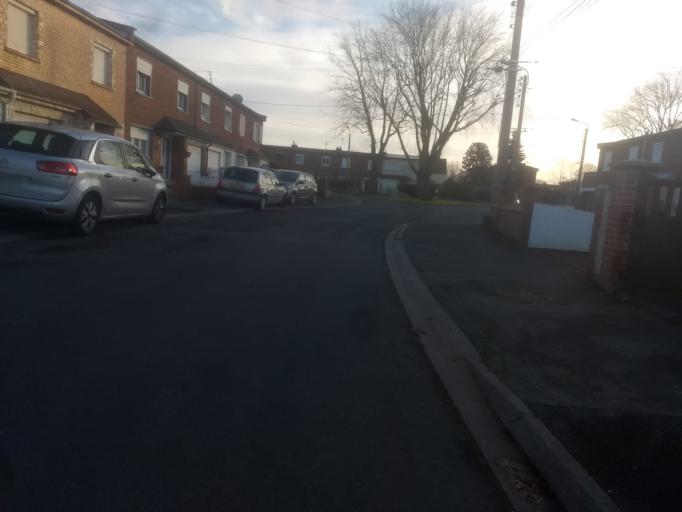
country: FR
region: Nord-Pas-de-Calais
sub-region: Departement du Pas-de-Calais
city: Beaurains
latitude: 50.2723
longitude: 2.7914
